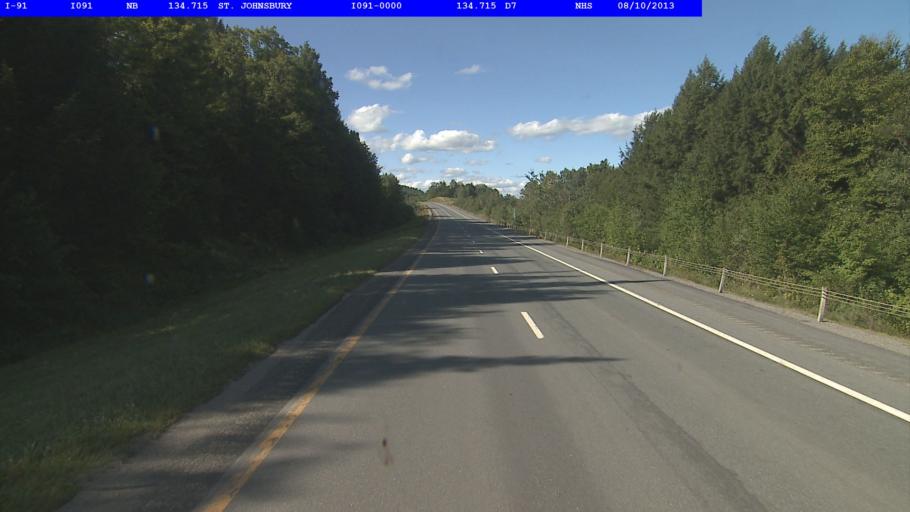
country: US
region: Vermont
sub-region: Caledonia County
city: Lyndon
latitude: 44.4846
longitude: -72.0215
